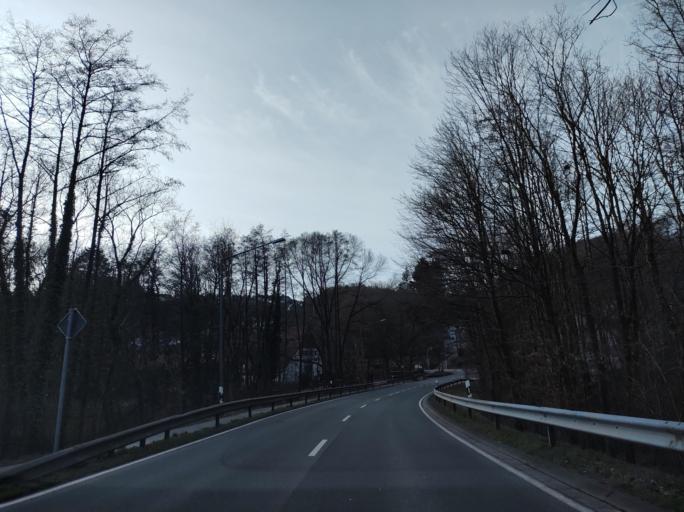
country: DE
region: North Rhine-Westphalia
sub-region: Regierungsbezirk Detmold
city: Detmold
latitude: 51.8944
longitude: 8.8801
